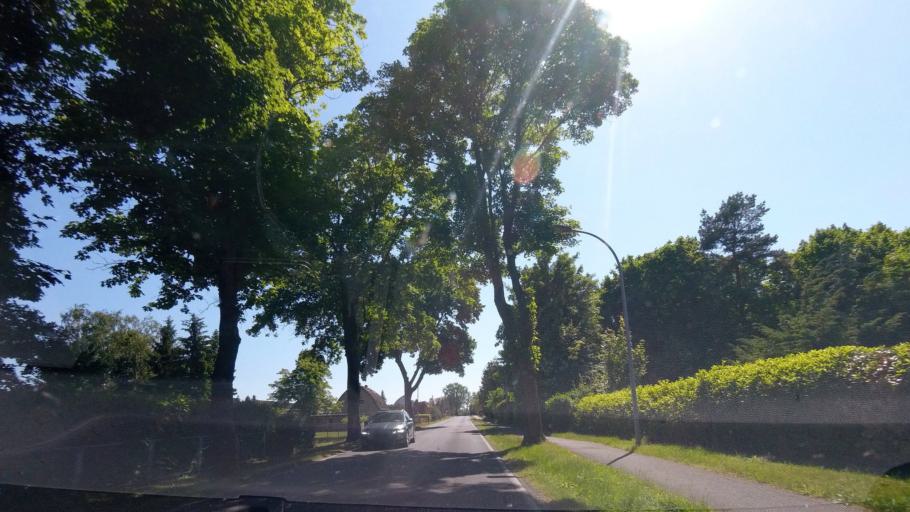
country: DE
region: Brandenburg
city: Gross Kreutz
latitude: 52.3941
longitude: 12.7114
